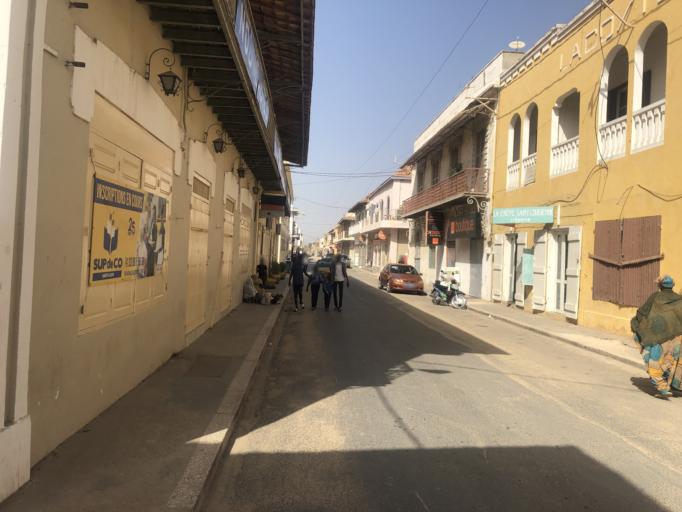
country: SN
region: Saint-Louis
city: Saint-Louis
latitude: 16.0275
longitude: -16.5047
